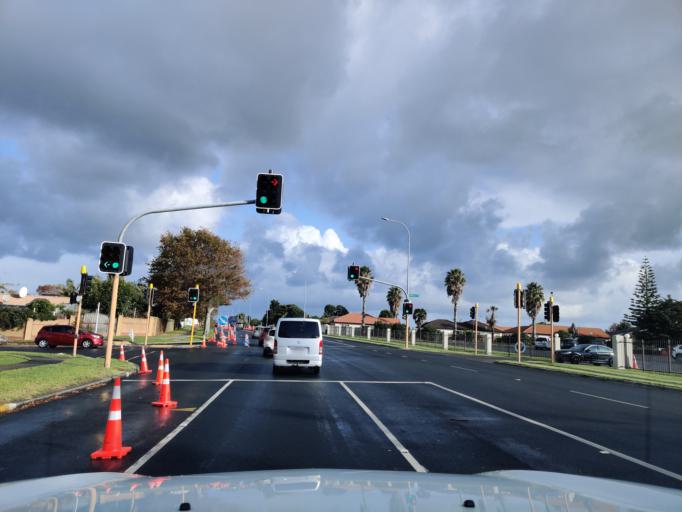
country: NZ
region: Auckland
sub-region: Auckland
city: Pakuranga
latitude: -36.9194
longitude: 174.9131
